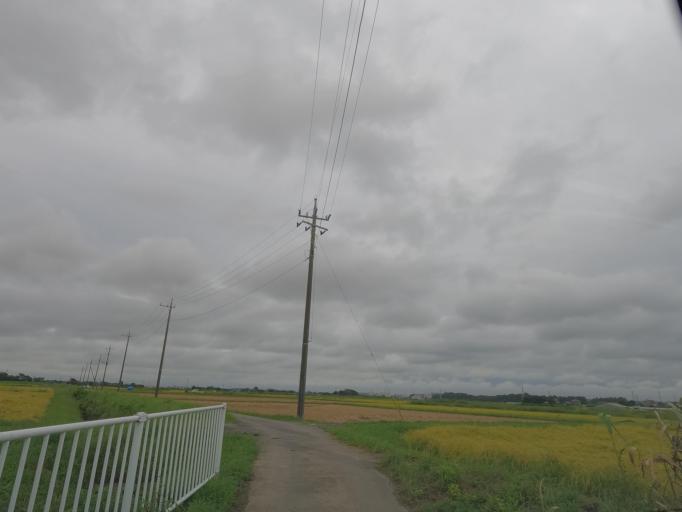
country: JP
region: Ibaraki
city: Toride
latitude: 35.9283
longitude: 140.0637
